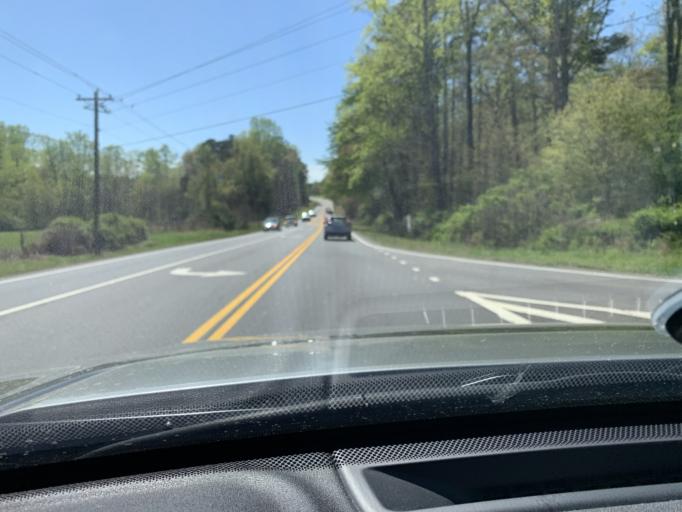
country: US
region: Georgia
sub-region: Fulton County
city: Milton
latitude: 34.1714
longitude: -84.2294
